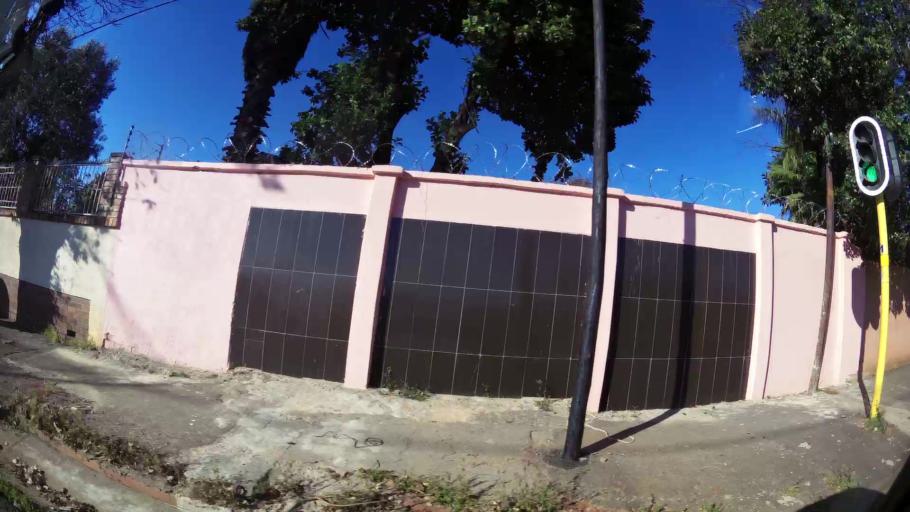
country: ZA
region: Gauteng
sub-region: City of Johannesburg Metropolitan Municipality
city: Johannesburg
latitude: -26.1915
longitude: 28.0918
